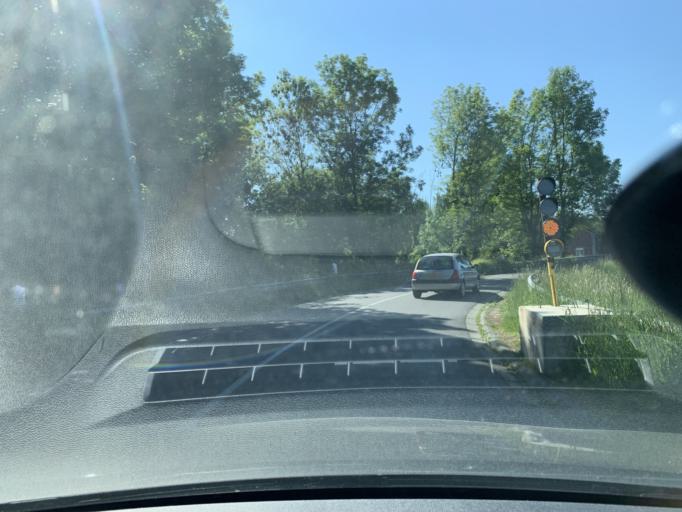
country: FR
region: Nord-Pas-de-Calais
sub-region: Departement du Nord
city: Rumilly-en-Cambresis
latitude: 50.1014
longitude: 3.2476
